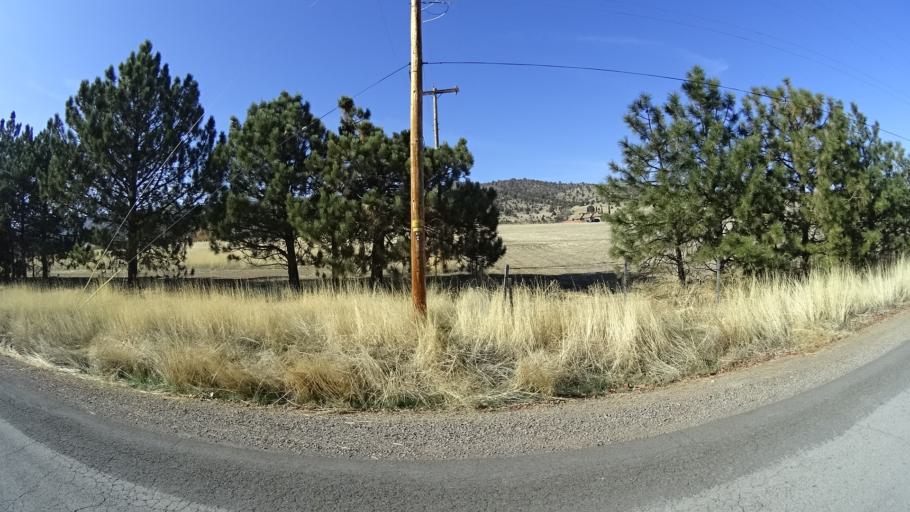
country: US
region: California
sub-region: Siskiyou County
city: Montague
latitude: 41.5937
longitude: -122.5414
